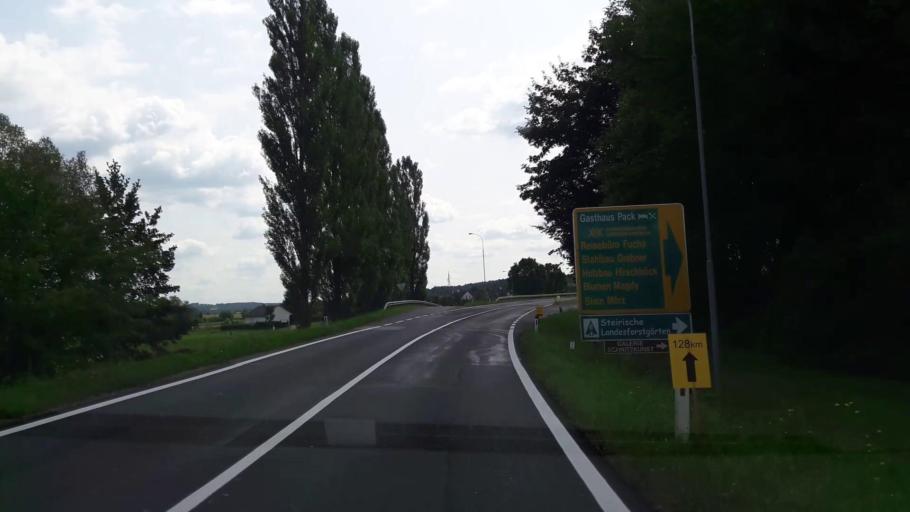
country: AT
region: Styria
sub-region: Politischer Bezirk Hartberg-Fuerstenfeld
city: Hartberg
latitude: 47.2711
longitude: 15.9709
